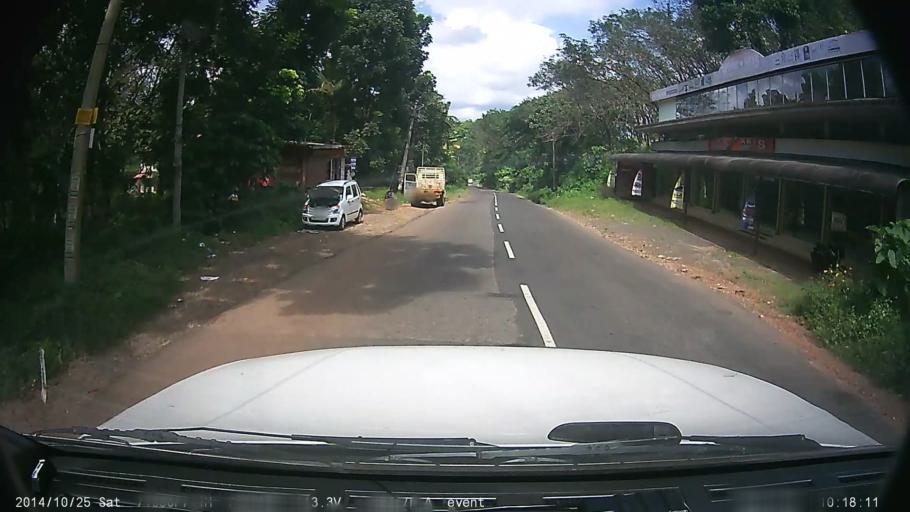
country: IN
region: Kerala
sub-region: Ernakulam
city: Piravam
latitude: 9.8826
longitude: 76.5936
